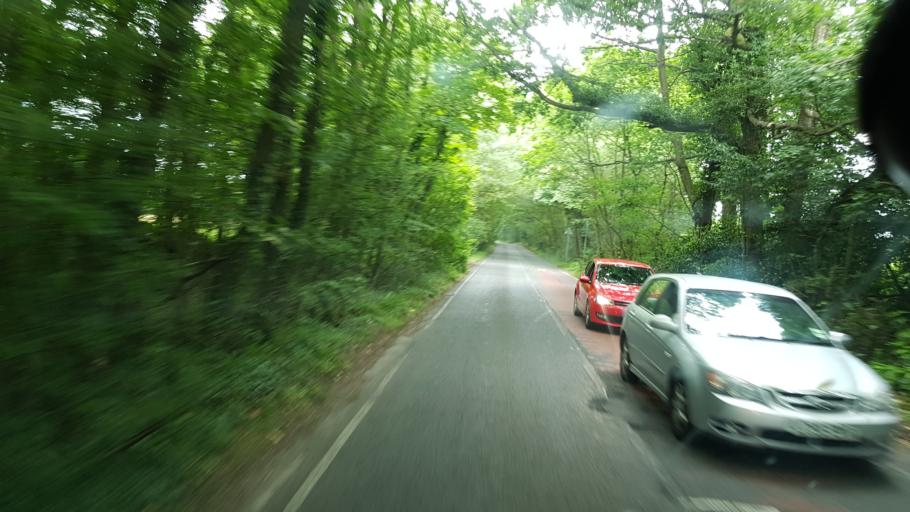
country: GB
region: England
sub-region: Surrey
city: Felbridge
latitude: 51.1261
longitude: -0.0348
